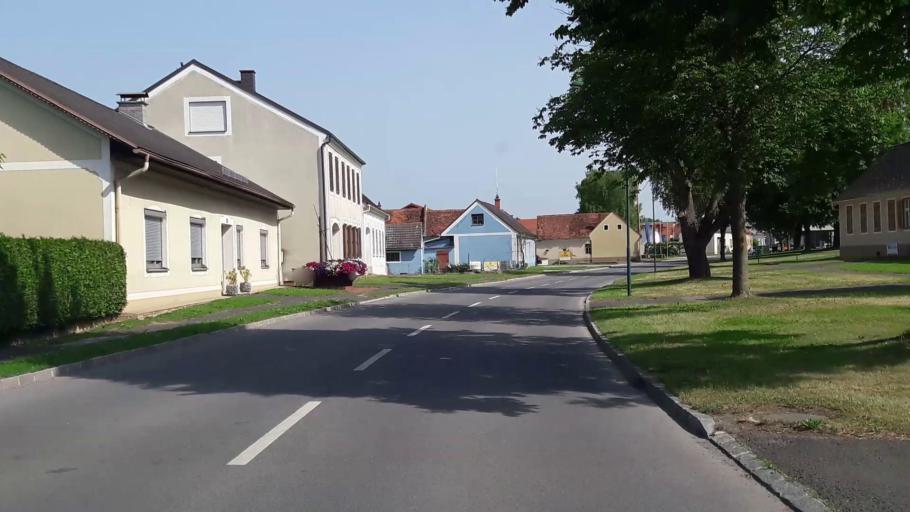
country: AT
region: Burgenland
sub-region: Politischer Bezirk Jennersdorf
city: Deutsch Kaltenbrunn
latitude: 47.0861
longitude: 16.1063
